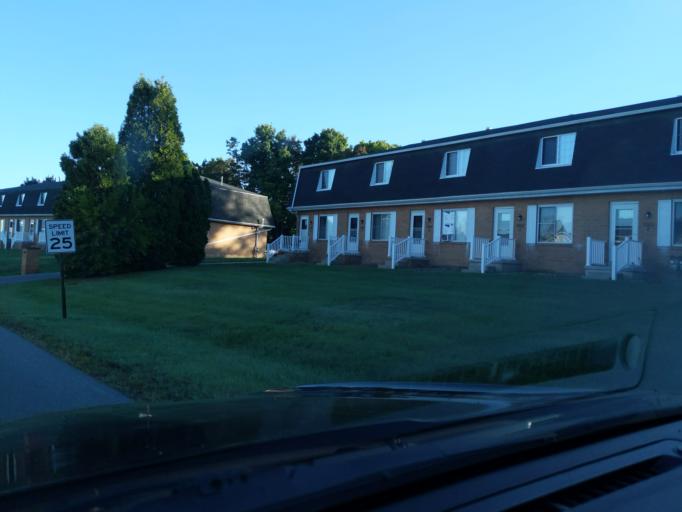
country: US
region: Pennsylvania
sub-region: Blair County
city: Greenwood
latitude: 40.5280
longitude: -78.3673
